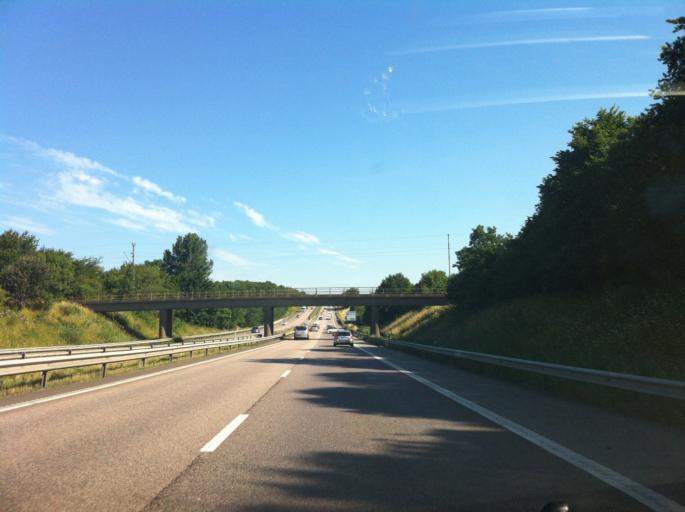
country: SE
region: Skane
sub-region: Helsingborg
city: Gantofta
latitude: 55.9932
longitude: 12.7801
